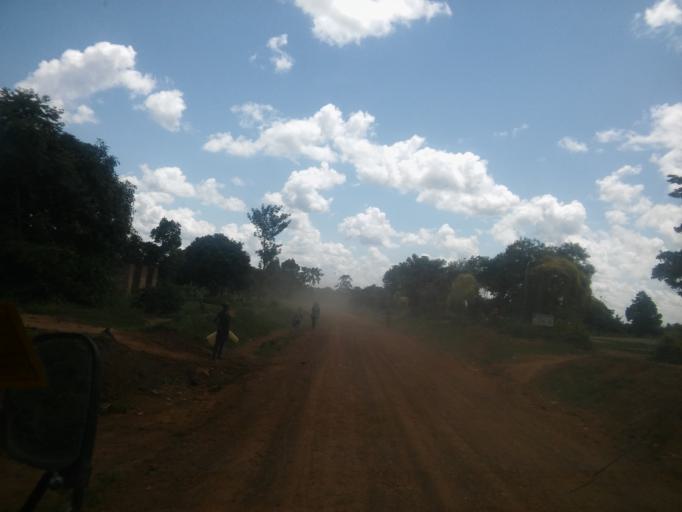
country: UG
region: Eastern Region
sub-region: Budaka District
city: Budaka
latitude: 1.1095
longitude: 33.9664
